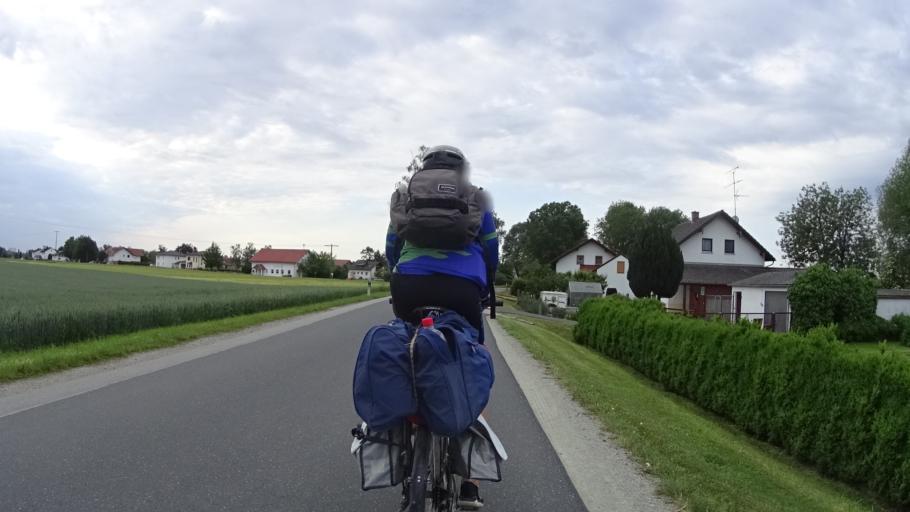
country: DE
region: Bavaria
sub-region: Lower Bavaria
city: Parkstetten
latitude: 48.9119
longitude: 12.6238
